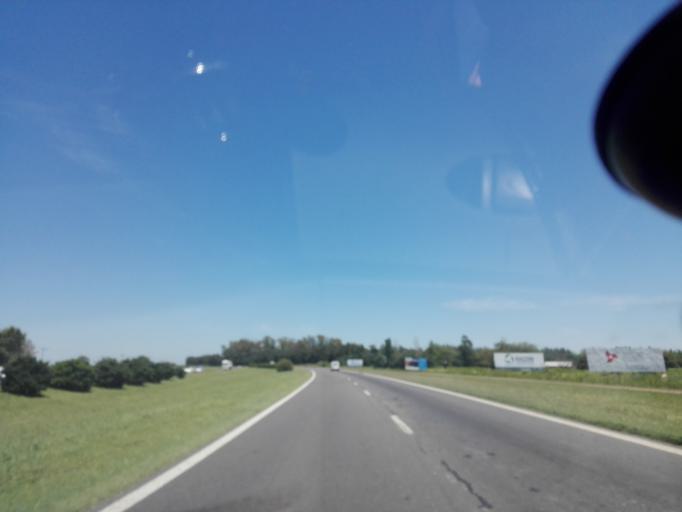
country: AR
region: Santa Fe
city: Funes
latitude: -32.9346
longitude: -60.8337
